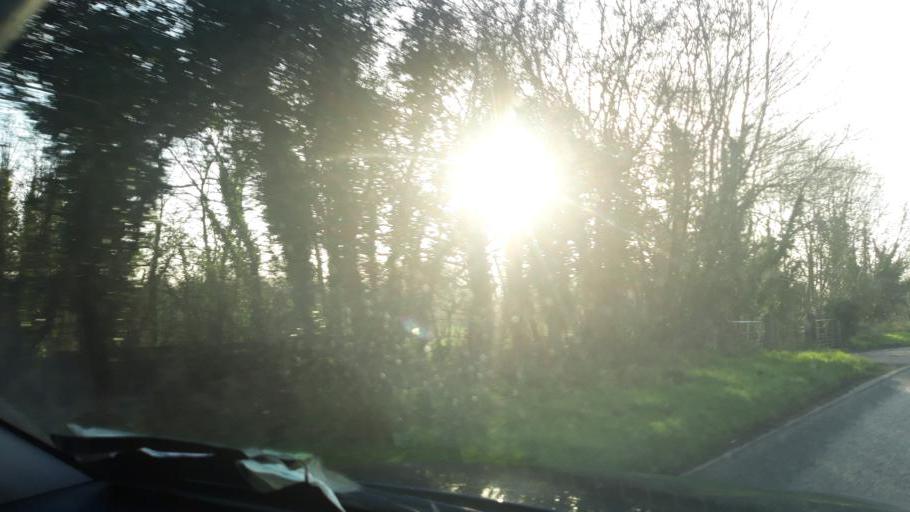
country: GB
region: Northern Ireland
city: Maghera
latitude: 54.8152
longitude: -6.7011
